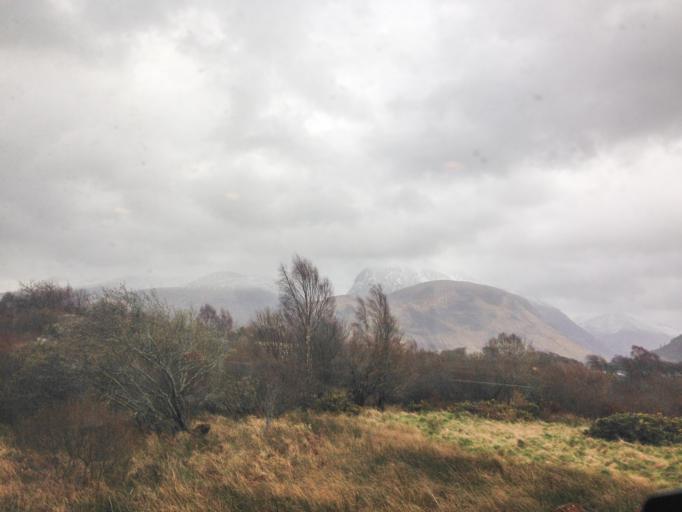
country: GB
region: Scotland
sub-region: Highland
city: Fort William
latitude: 56.8435
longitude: -5.1144
